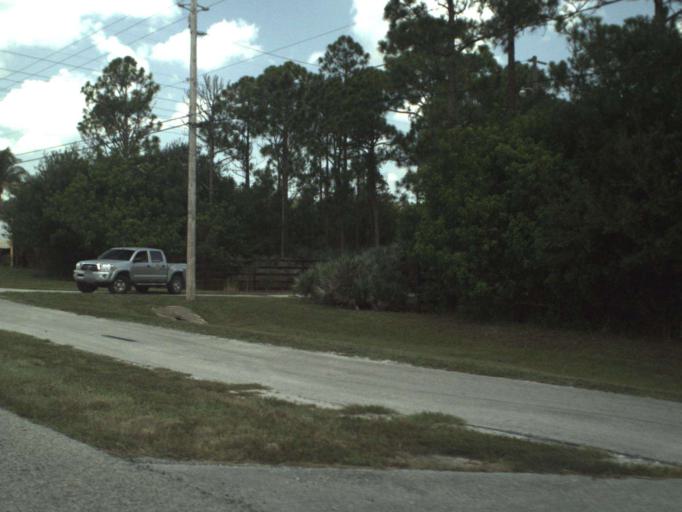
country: US
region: Florida
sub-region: Saint Lucie County
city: Fort Pierce South
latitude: 27.4061
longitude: -80.4326
